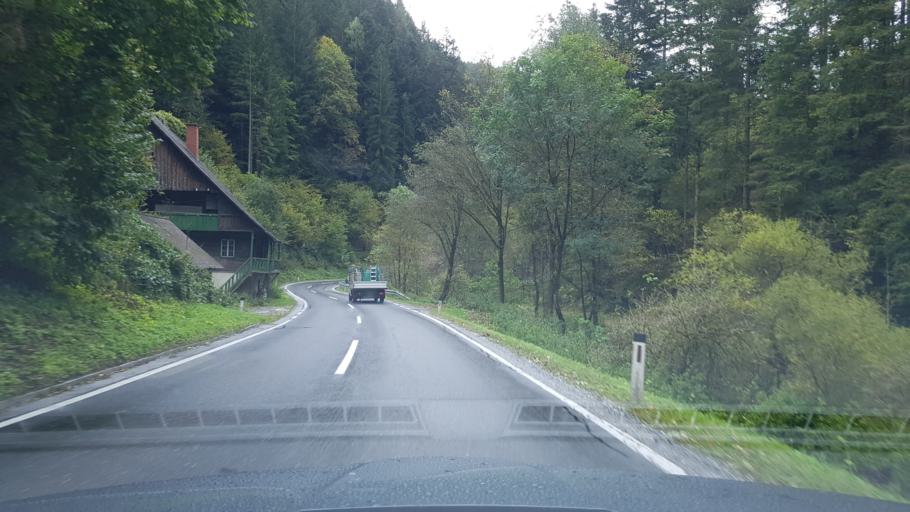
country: AT
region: Styria
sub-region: Politischer Bezirk Voitsberg
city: Salla
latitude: 47.1108
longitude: 15.0097
